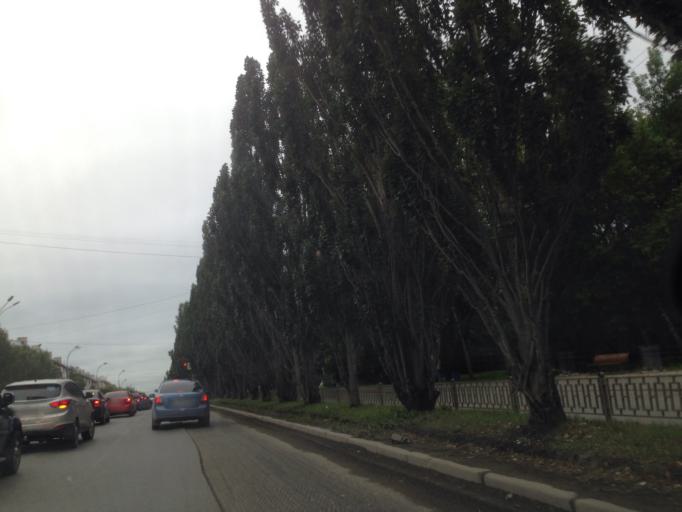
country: RU
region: Sverdlovsk
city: Yekaterinburg
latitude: 56.8341
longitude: 60.6347
